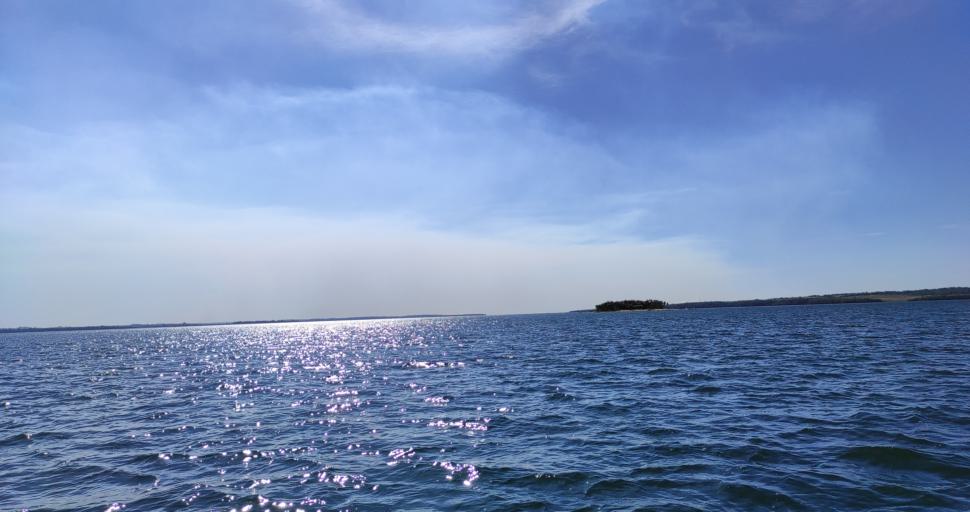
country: PY
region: Itapua
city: San Juan del Parana
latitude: -27.3439
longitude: -55.9424
